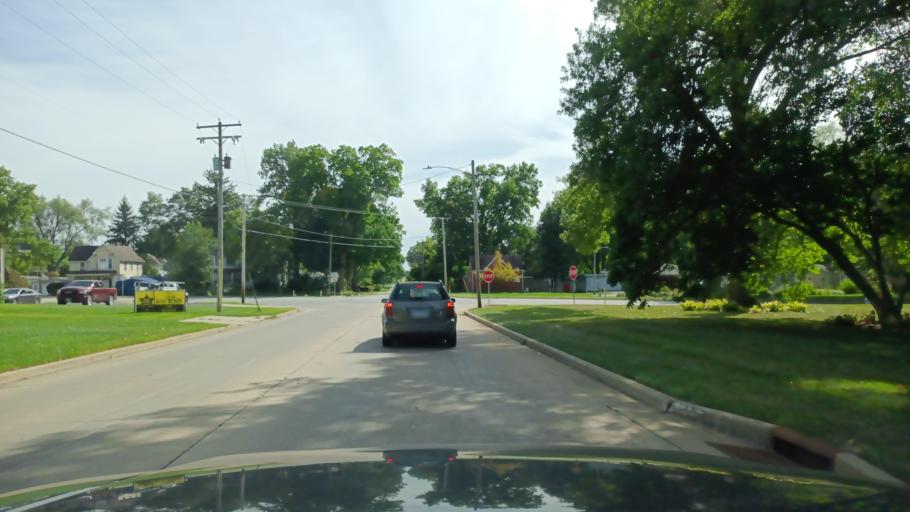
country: US
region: Illinois
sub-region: Knox County
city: Knoxville
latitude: 40.9089
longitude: -90.2895
